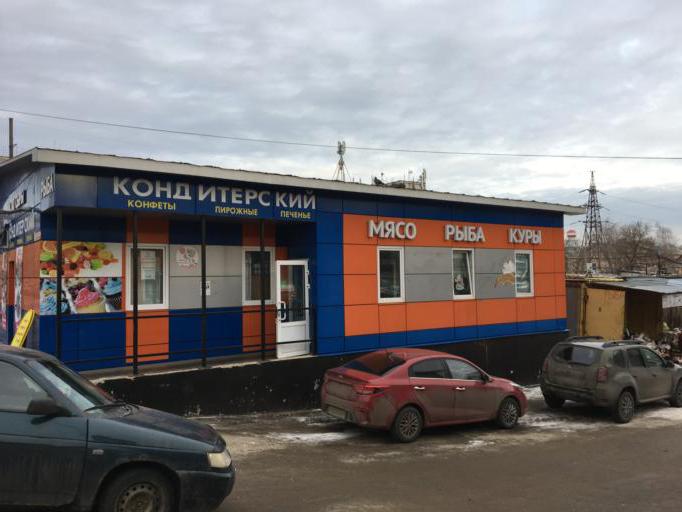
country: RU
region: Nizjnij Novgorod
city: Nizhniy Novgorod
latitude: 56.2902
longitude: 43.9870
